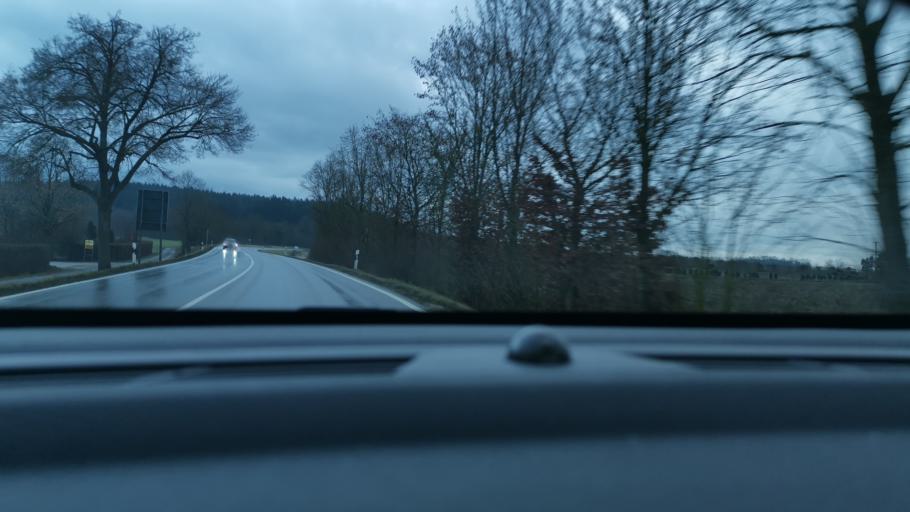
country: DE
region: Bavaria
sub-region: Swabia
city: Petersdorf
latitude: 48.4923
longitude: 11.0095
